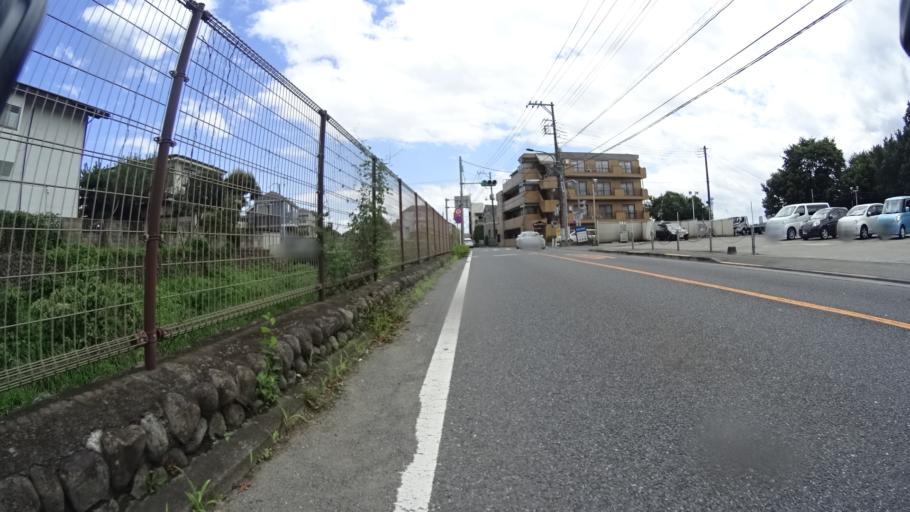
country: JP
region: Tokyo
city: Fussa
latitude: 35.7346
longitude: 139.3273
